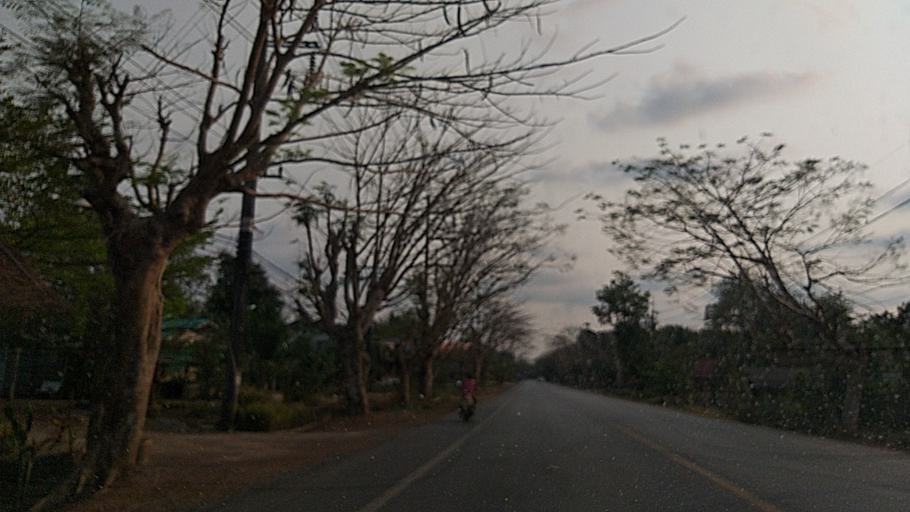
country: TH
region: Trat
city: Khao Saming
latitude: 12.2964
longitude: 102.3343
